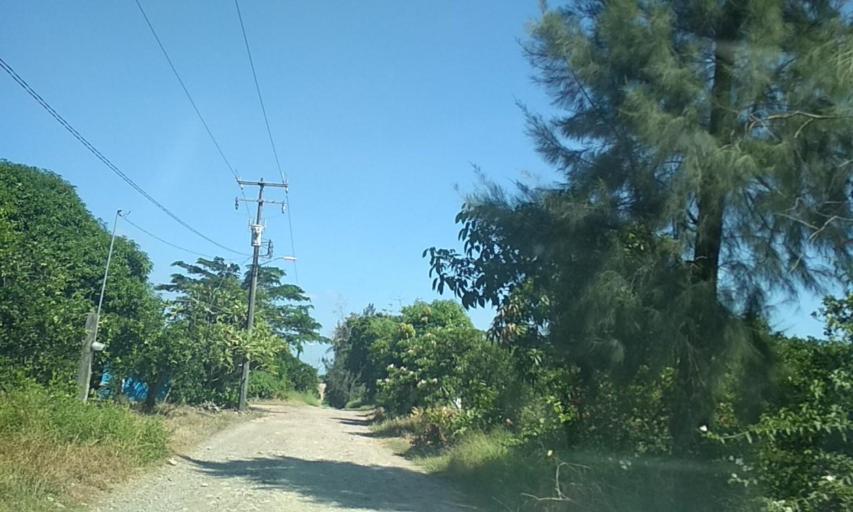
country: MX
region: Veracruz
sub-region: Martinez de la Torre
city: La Union Paso Largo
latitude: 20.1519
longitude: -96.9986
